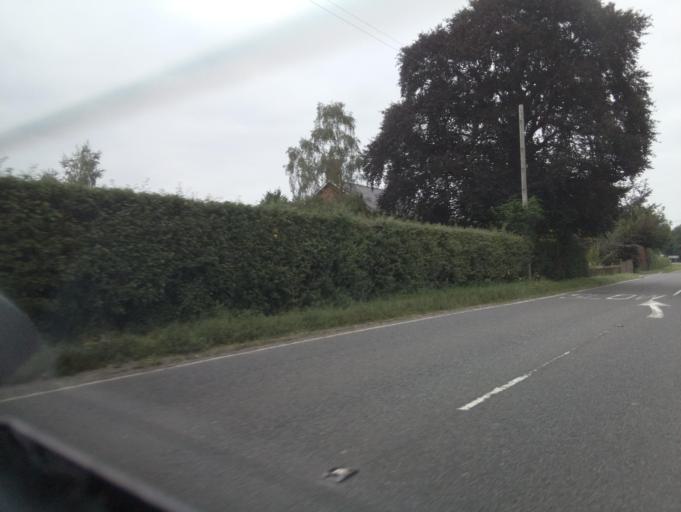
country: GB
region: England
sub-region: Shropshire
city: Astley
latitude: 52.7626
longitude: -2.6841
